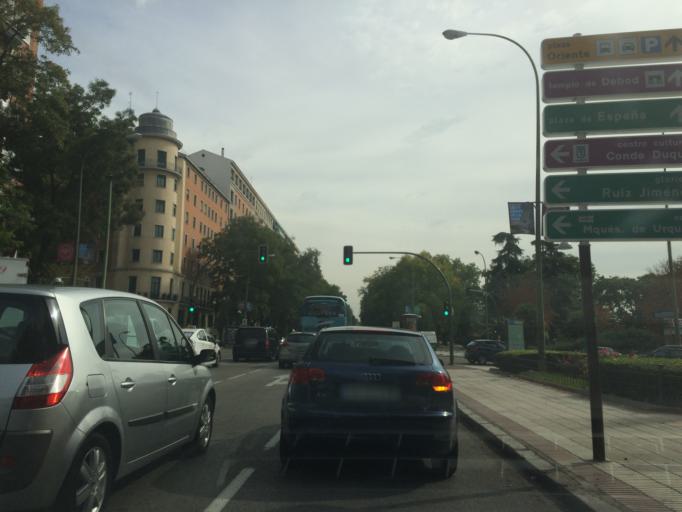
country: ES
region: Madrid
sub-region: Provincia de Madrid
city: Moncloa-Aravaca
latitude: 40.4293
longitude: -3.7221
